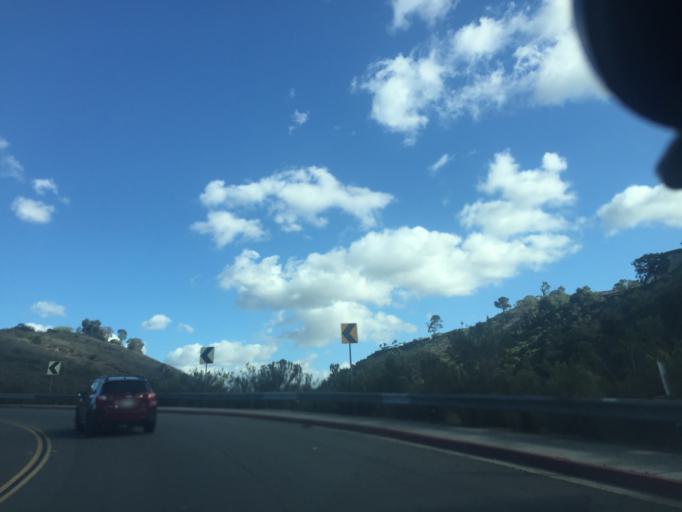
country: US
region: California
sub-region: San Diego County
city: La Mesa
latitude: 32.7837
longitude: -117.0854
